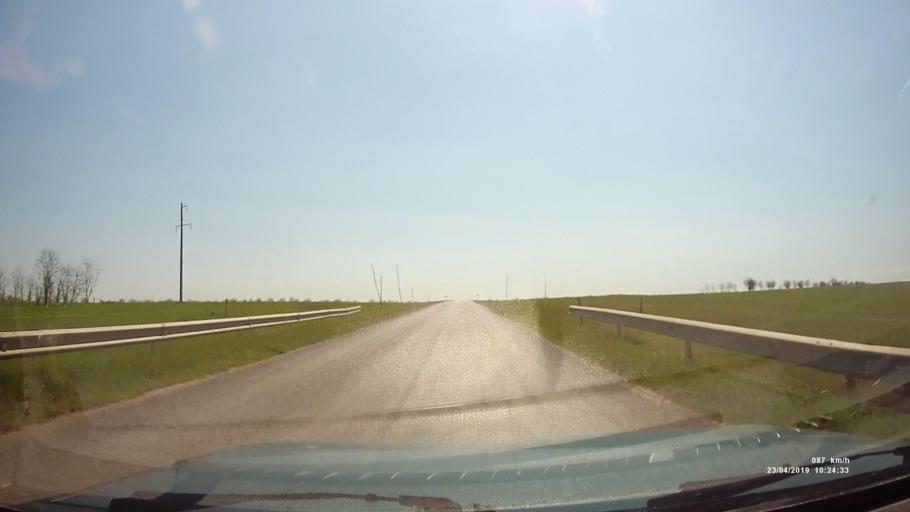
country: RU
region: Rostov
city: Sovetskoye
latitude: 46.6380
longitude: 42.4433
